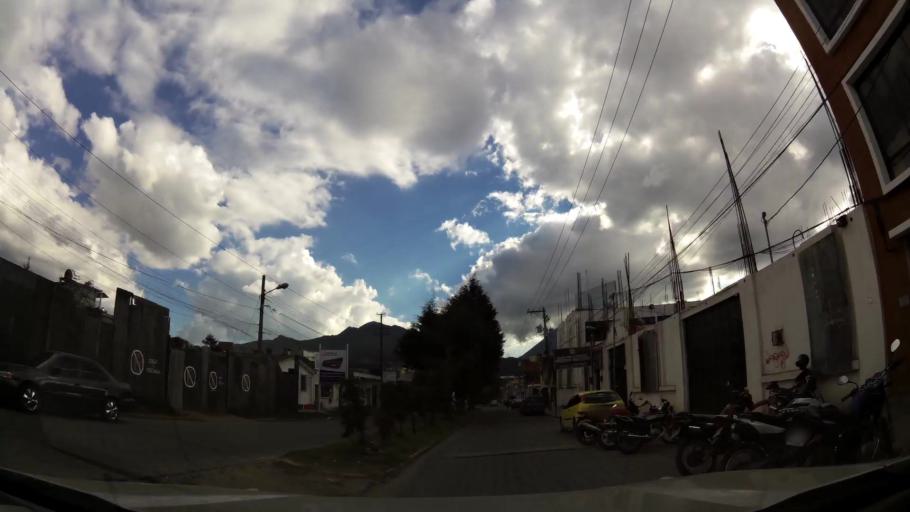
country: GT
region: Quetzaltenango
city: Quetzaltenango
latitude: 14.8447
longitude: -91.5251
